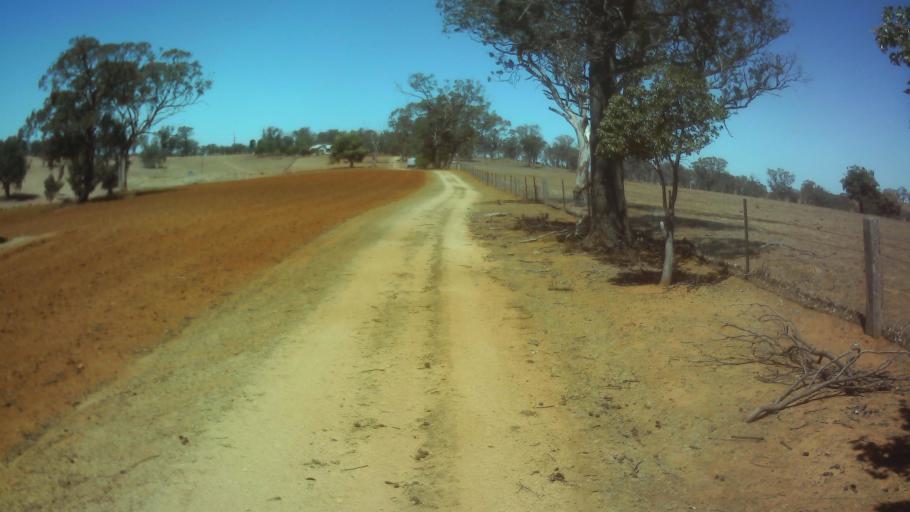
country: AU
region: New South Wales
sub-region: Cowra
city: Cowra
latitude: -33.9065
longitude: 148.5079
